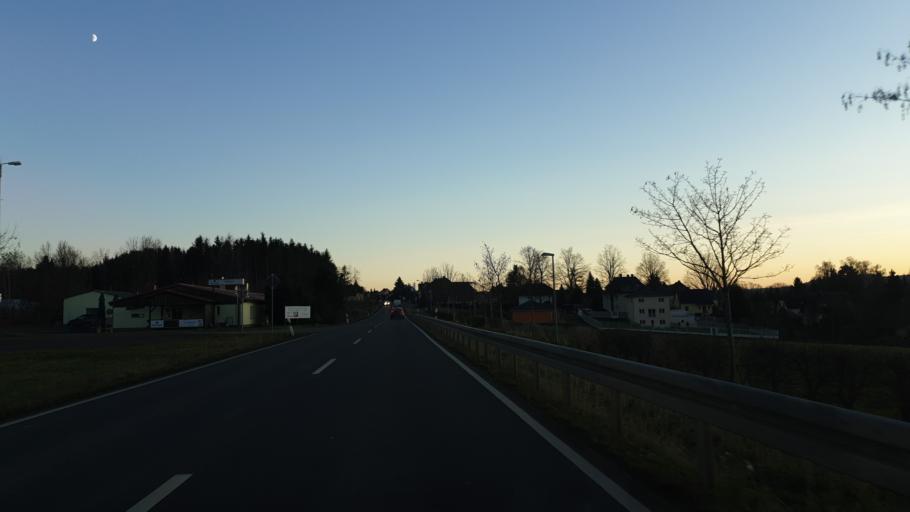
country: DE
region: Saxony
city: Oberlungwitz
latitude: 50.7722
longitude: 12.7089
